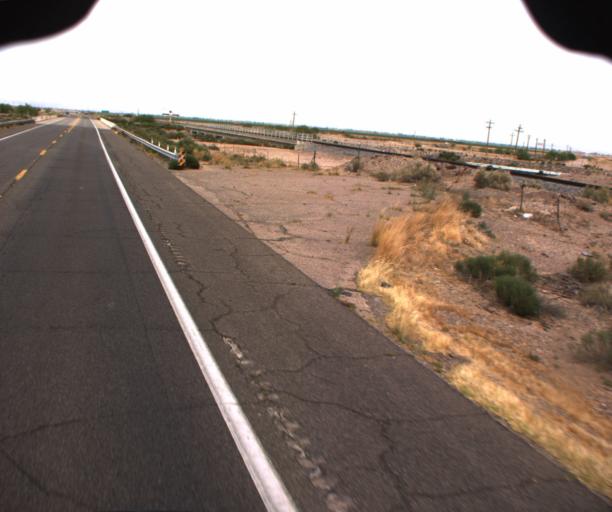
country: US
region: Arizona
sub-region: Maricopa County
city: Sun Lakes
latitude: 33.1670
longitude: -111.7892
